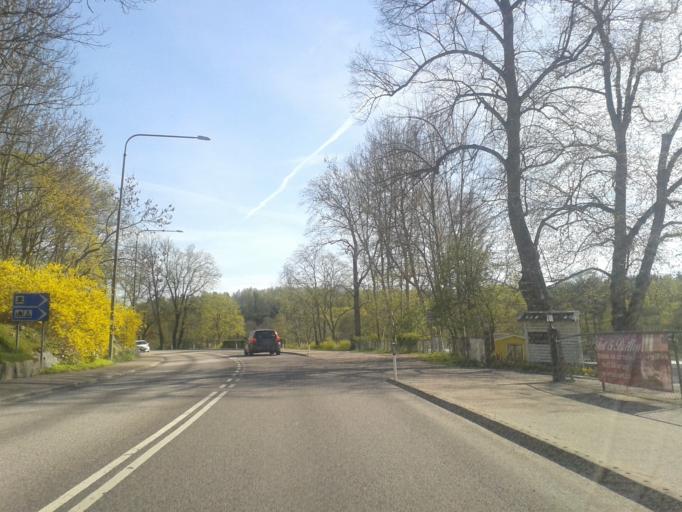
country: SE
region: Vaestra Goetaland
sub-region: Kungalvs Kommun
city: Kungalv
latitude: 57.8625
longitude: 11.9965
